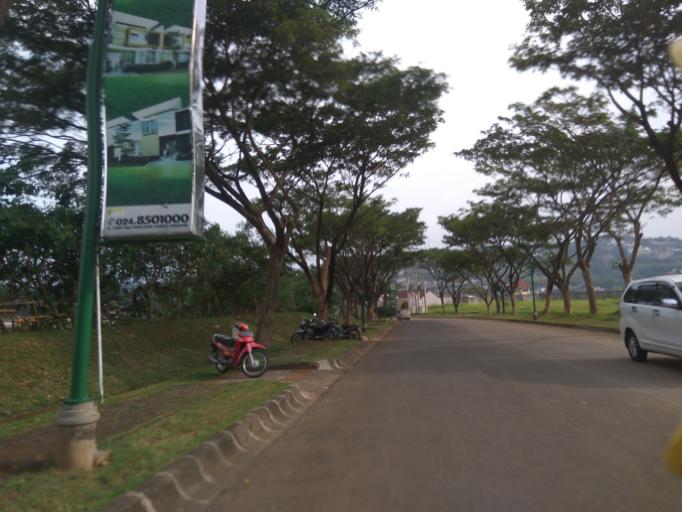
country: ID
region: Central Java
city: Semarang
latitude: -7.0322
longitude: 110.4352
